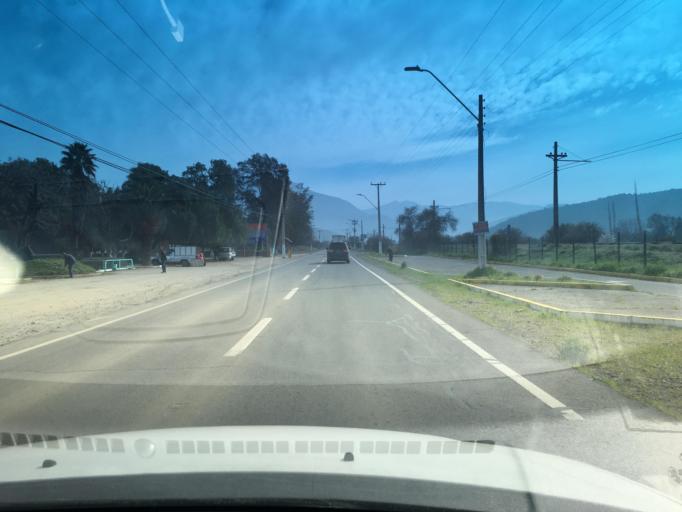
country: CL
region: Santiago Metropolitan
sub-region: Provincia de Chacabuco
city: Lampa
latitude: -33.1155
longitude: -70.9267
